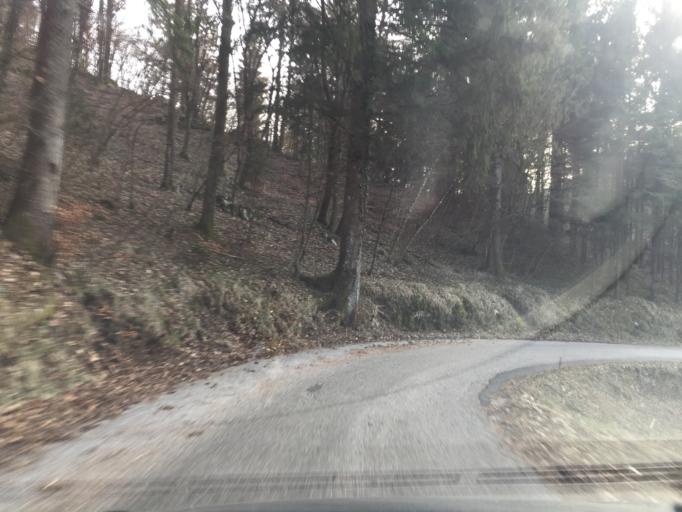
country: SI
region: Kanal
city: Kanal
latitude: 46.0568
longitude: 13.6670
